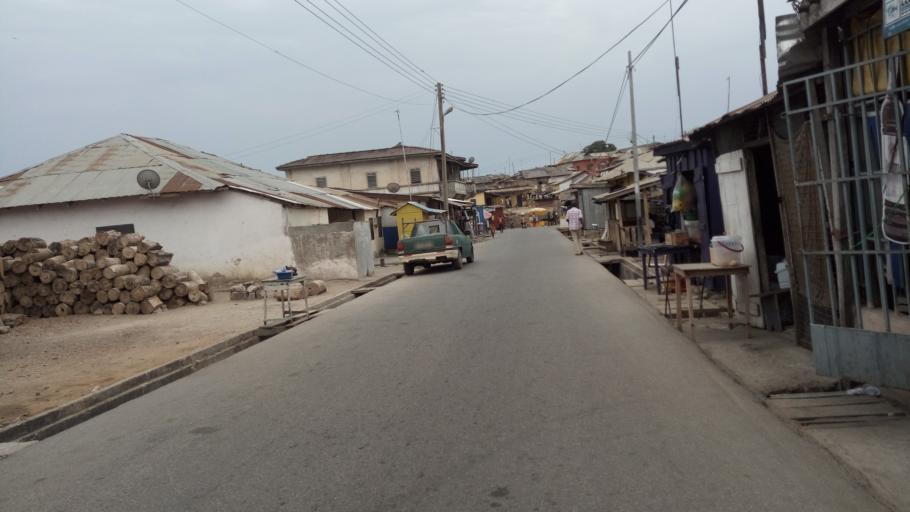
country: GH
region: Central
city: Winneba
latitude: 5.3408
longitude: -0.6216
